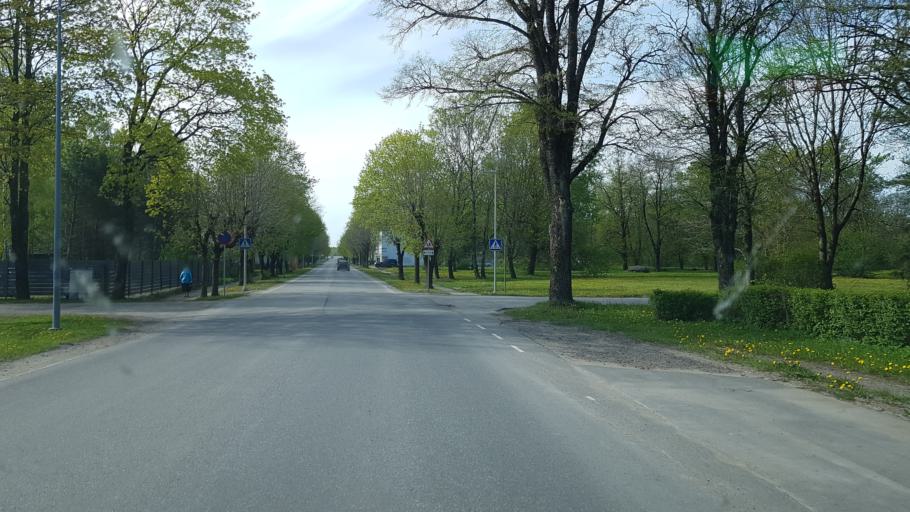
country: EE
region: Ida-Virumaa
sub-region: Kivioli linn
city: Kivioli
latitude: 59.3581
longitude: 26.9668
